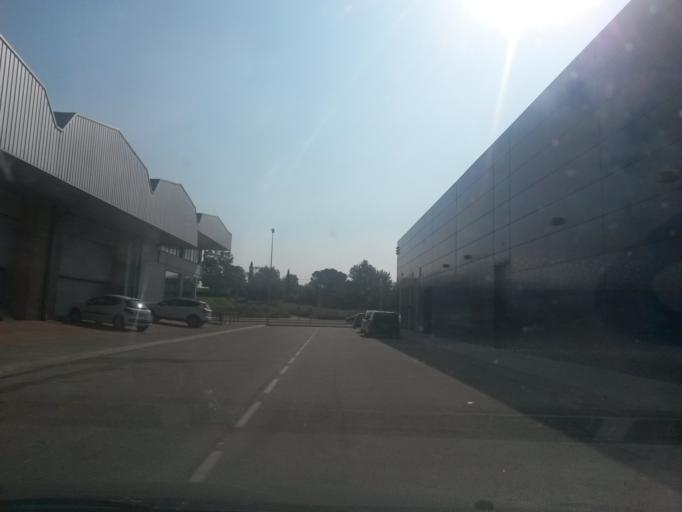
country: ES
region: Catalonia
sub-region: Provincia de Girona
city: Fornells de la Selva
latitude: 41.9383
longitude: 2.8000
